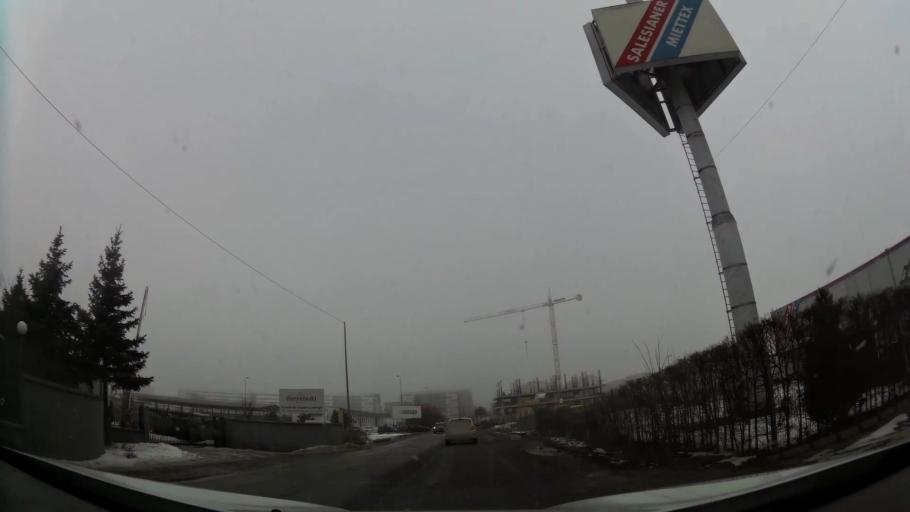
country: RO
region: Ilfov
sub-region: Comuna Chiajna
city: Chiajna
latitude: 44.4387
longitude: 25.9873
